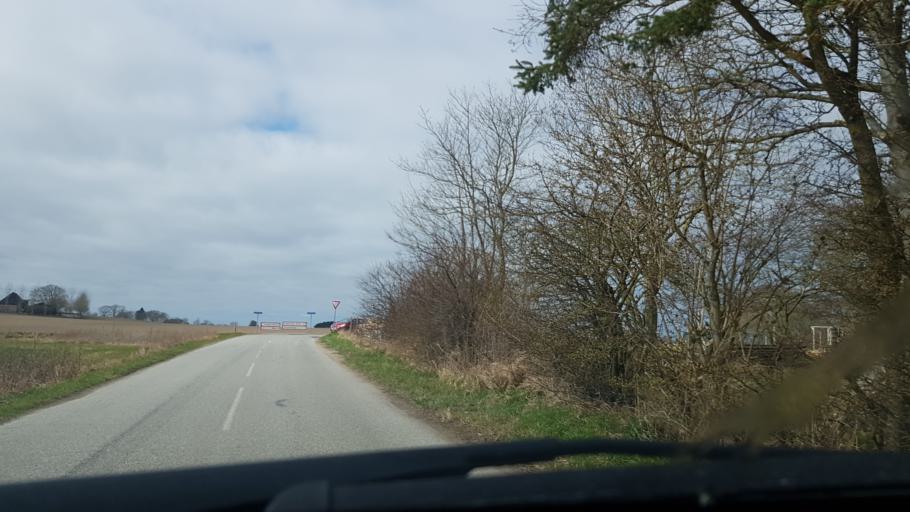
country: DK
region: Zealand
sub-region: Odsherred Kommune
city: Hojby
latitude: 55.9190
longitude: 11.5694
